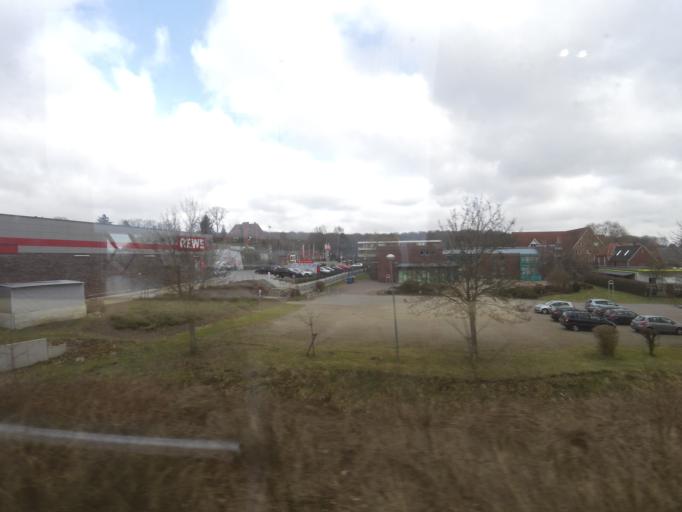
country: DE
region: Lower Saxony
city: Seevetal
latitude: 53.4082
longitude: 9.9931
